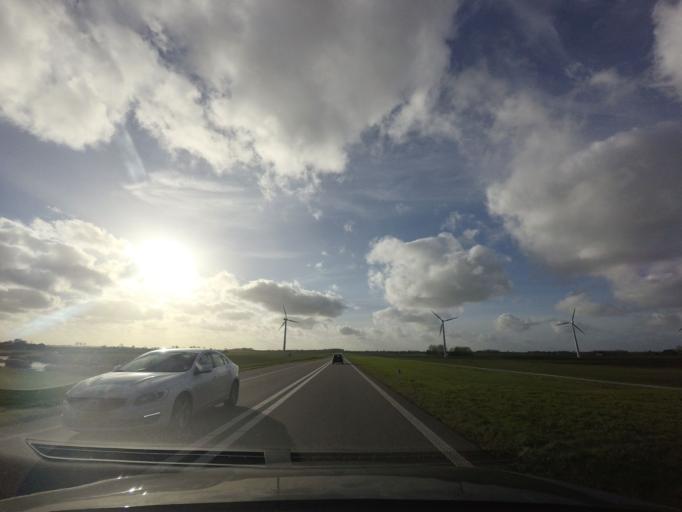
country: NL
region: North Holland
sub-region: Gemeente Opmeer
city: Opmeer
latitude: 52.7633
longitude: 4.9454
